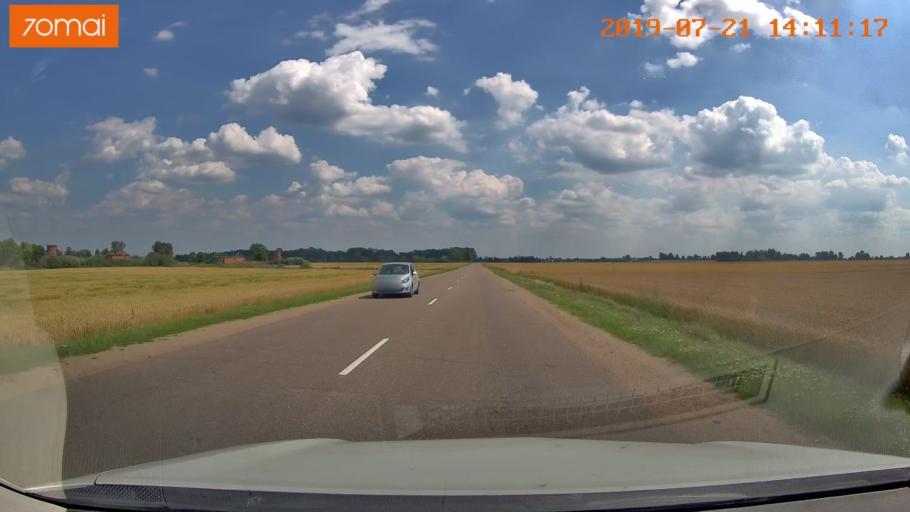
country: BY
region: Grodnenskaya
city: Karelichy
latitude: 53.6586
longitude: 26.1490
